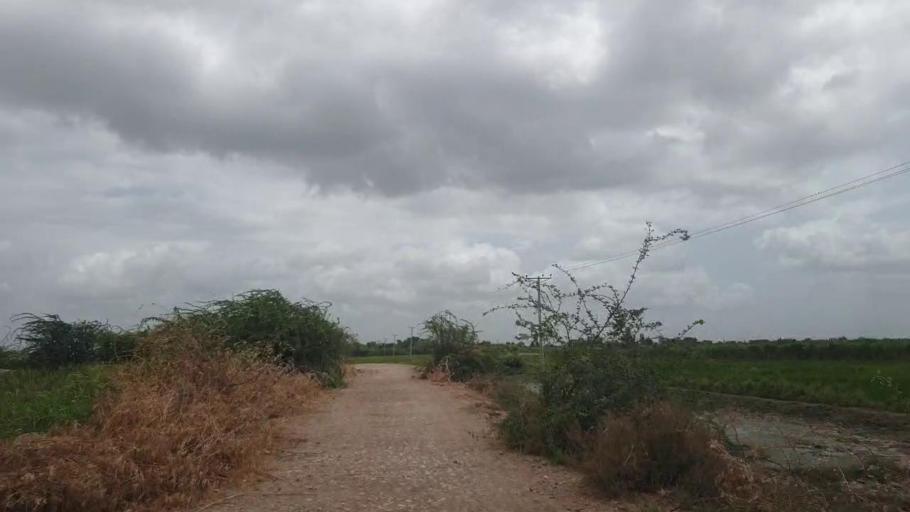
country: PK
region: Sindh
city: Badin
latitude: 24.6273
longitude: 68.9466
